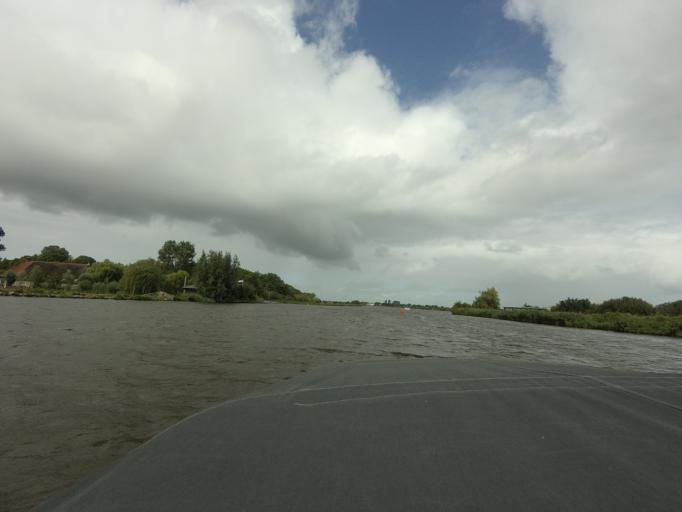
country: NL
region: Friesland
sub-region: Gemeente Boarnsterhim
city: Warten
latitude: 53.1384
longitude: 5.9148
